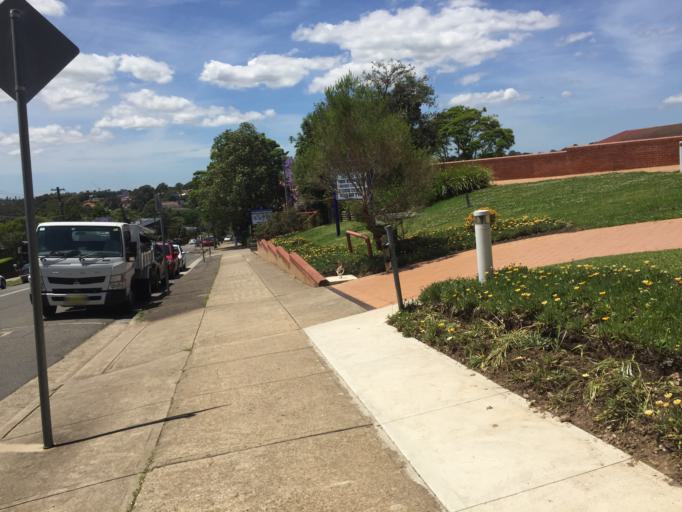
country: AU
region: New South Wales
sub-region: Ryde
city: Denistone
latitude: -33.7896
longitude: 151.0781
